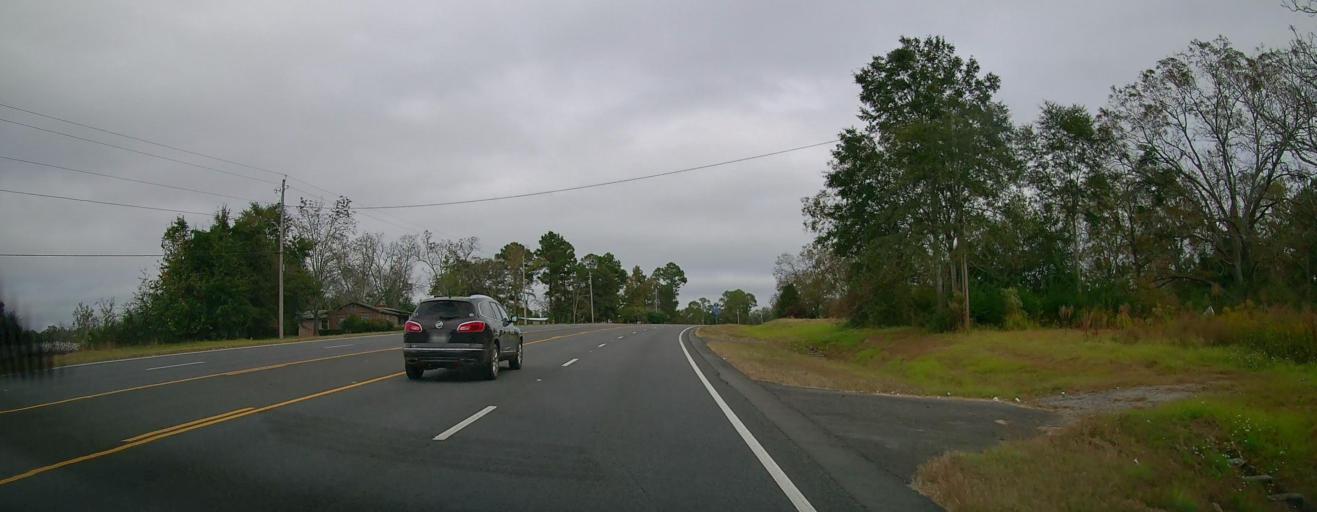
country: US
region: Georgia
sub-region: Thomas County
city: Thomasville
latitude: 30.9392
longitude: -83.9093
